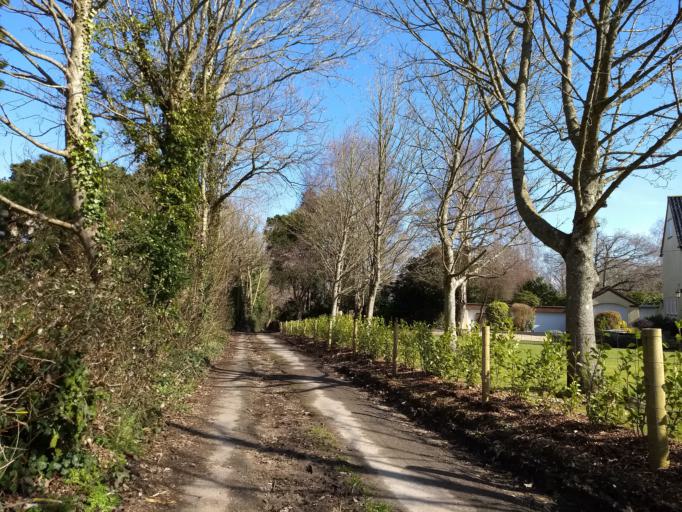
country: GB
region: England
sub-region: Isle of Wight
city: Seaview
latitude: 50.7113
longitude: -1.1070
